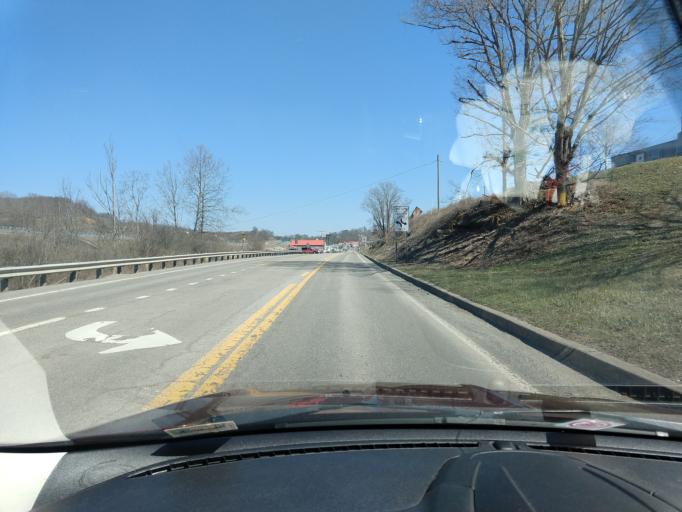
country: US
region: West Virginia
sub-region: Braxton County
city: Sutton
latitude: 38.6956
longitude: -80.6690
